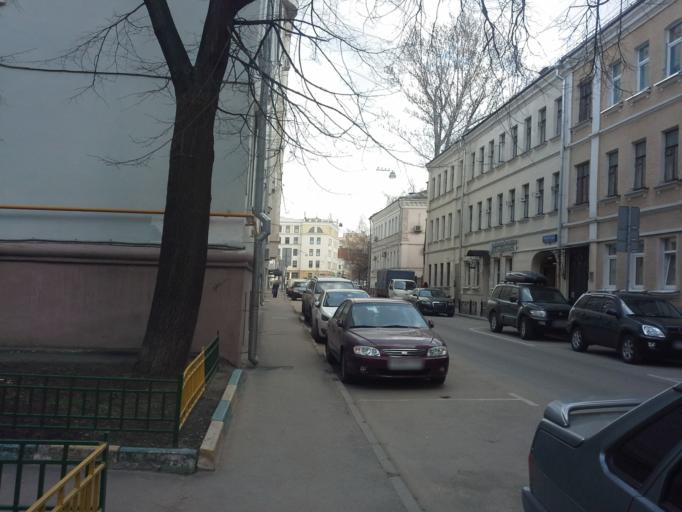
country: RU
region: Moscow
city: Moscow
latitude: 55.7690
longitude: 37.6289
